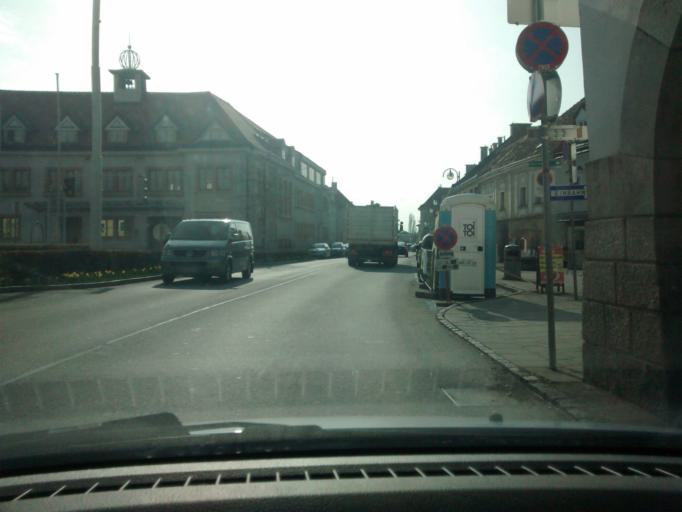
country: AT
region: Lower Austria
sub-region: Politischer Bezirk Baden
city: Traiskirchen
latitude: 48.0138
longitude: 16.2947
